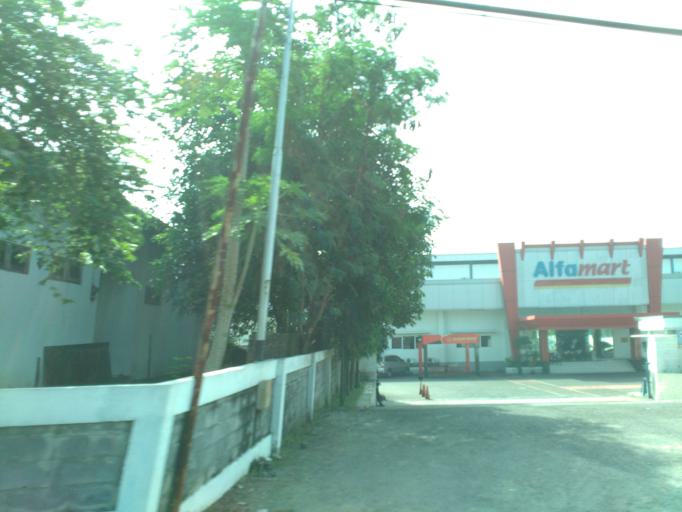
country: ID
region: Central Java
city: Delanggu
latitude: -7.6386
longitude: 110.6911
